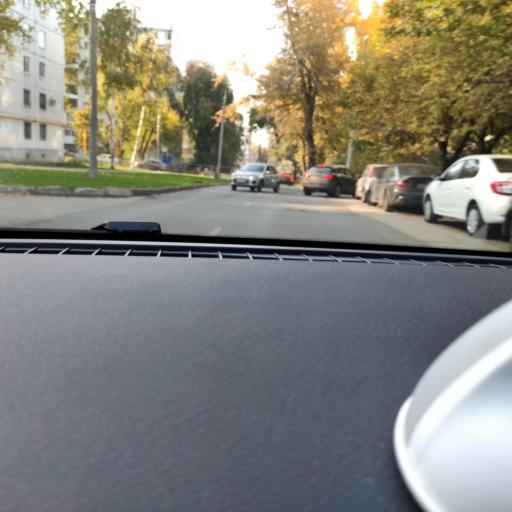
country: RU
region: Samara
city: Samara
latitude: 53.2084
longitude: 50.1434
